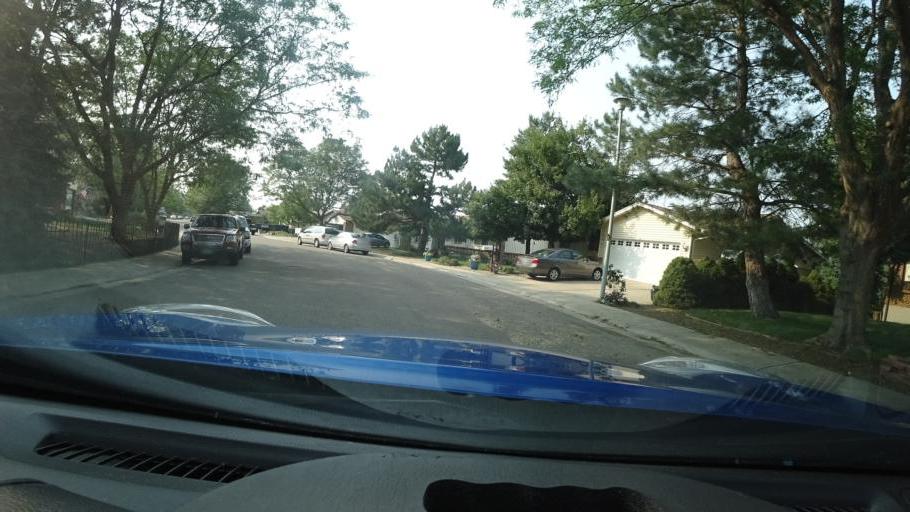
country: US
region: Colorado
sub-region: Adams County
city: Aurora
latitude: 39.6680
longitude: -104.7815
